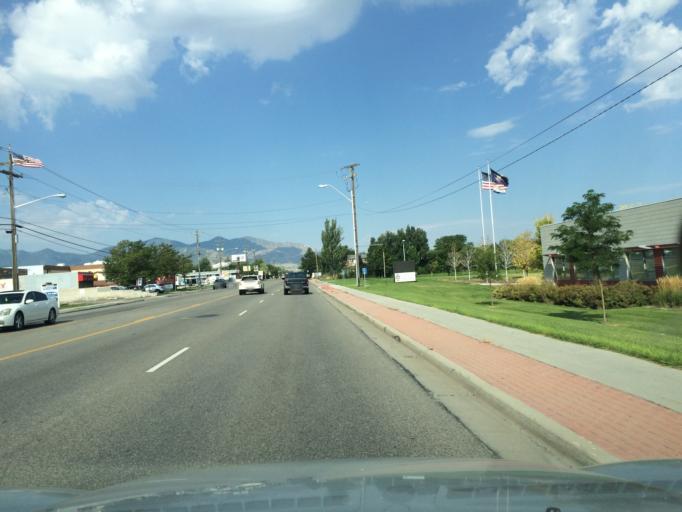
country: US
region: Utah
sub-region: Salt Lake County
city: West Valley City
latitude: 40.6967
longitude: -111.9990
